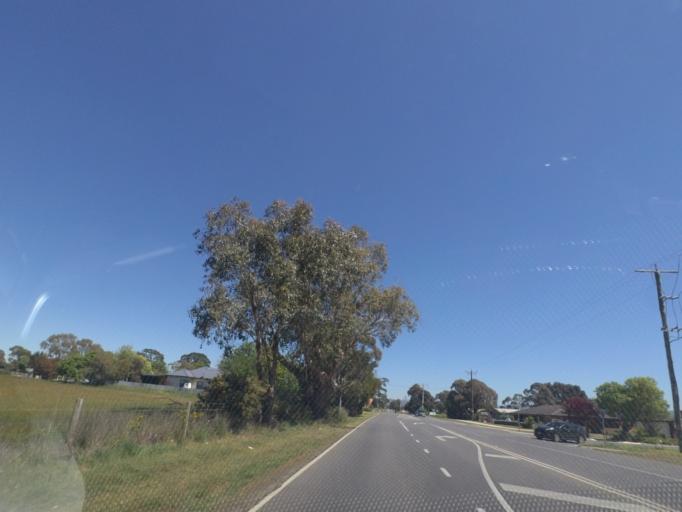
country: AU
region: Victoria
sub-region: Whittlesea
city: Whittlesea
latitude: -37.2950
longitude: 144.9418
